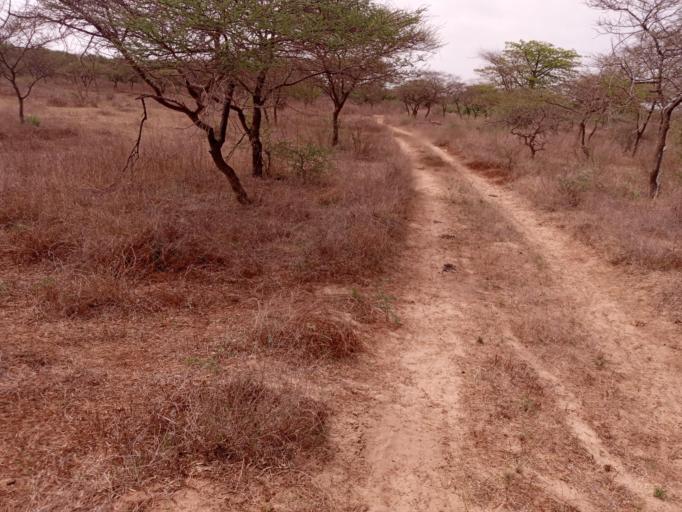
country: SN
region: Saint-Louis
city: Saint-Louis
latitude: 15.9176
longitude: -16.4534
